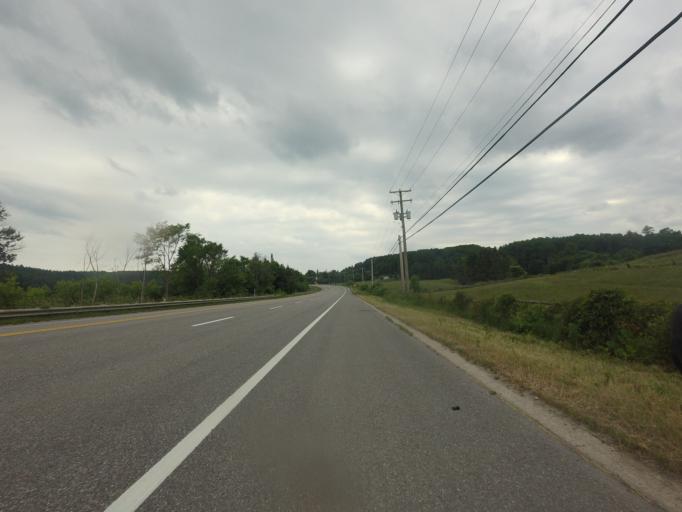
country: CA
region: Quebec
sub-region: Outaouais
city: Wakefield
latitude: 45.7173
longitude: -75.9151
